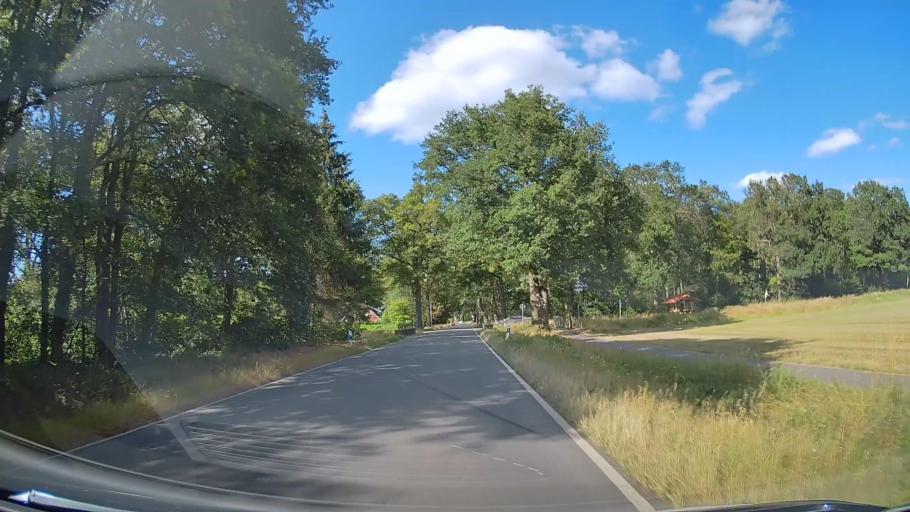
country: DE
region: Lower Saxony
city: Menslage
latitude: 52.6510
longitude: 7.8119
